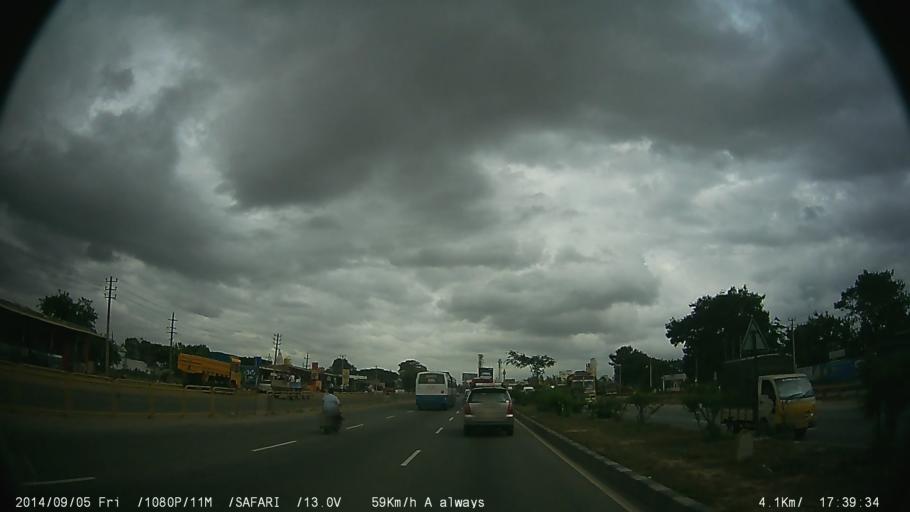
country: IN
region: Karnataka
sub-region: Bangalore Urban
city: Anekal
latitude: 12.7902
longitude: 77.7328
